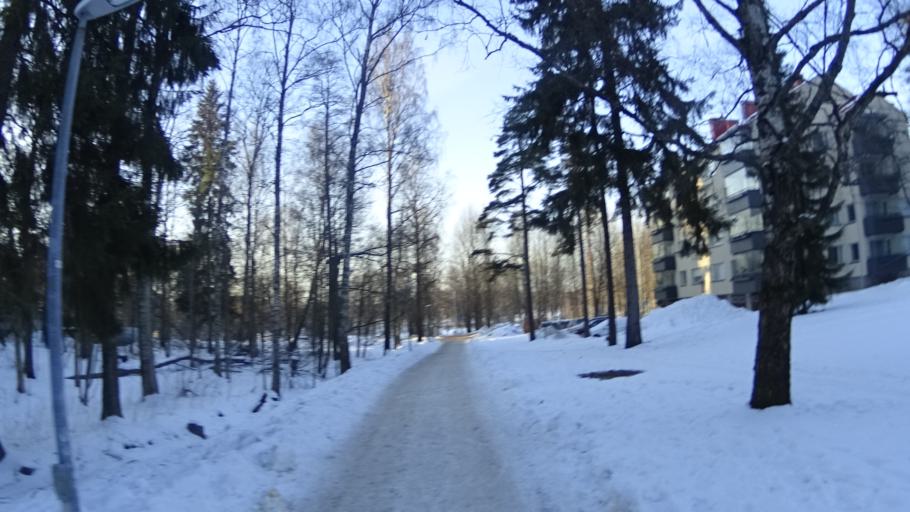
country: FI
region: Uusimaa
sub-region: Helsinki
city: Teekkarikylae
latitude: 60.2087
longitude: 24.8684
